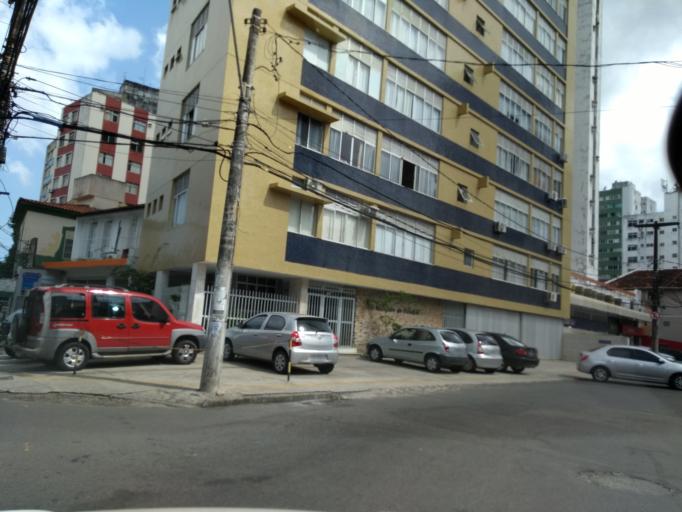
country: BR
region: Bahia
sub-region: Salvador
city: Salvador
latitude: -13.0050
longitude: -38.5301
